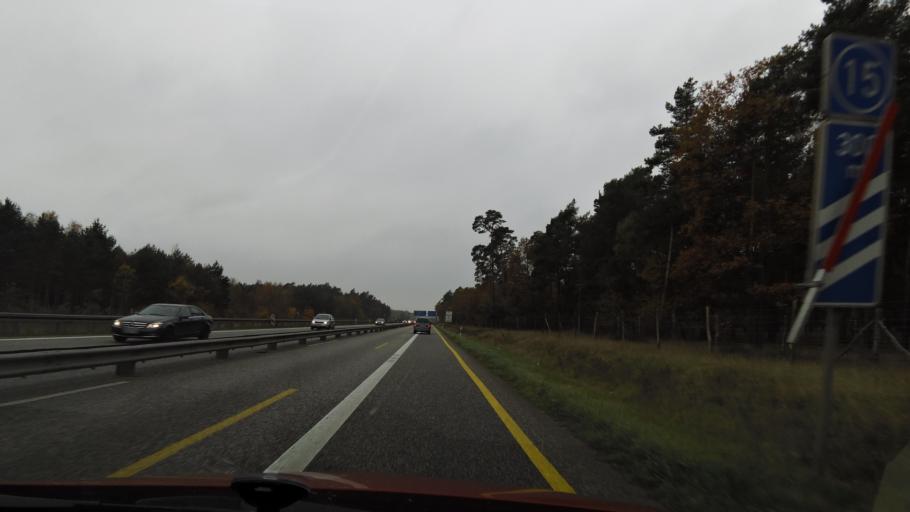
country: DE
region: Brandenburg
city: Ludwigsfelde
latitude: 52.3015
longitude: 13.2216
